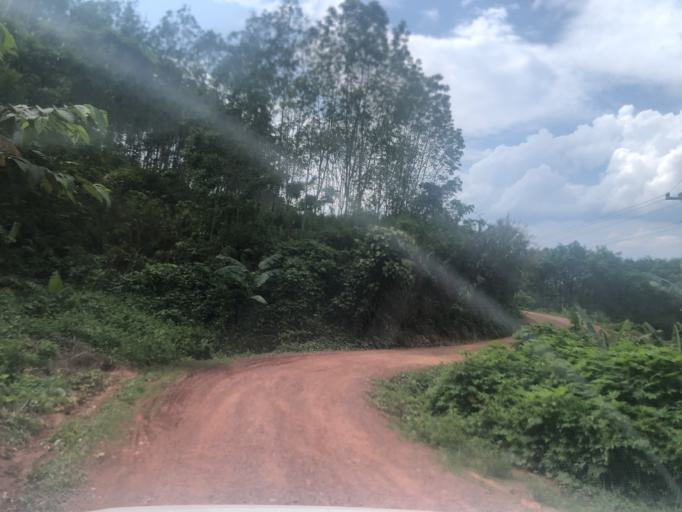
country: LA
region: Oudomxai
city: Muang La
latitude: 21.2482
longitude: 101.9337
